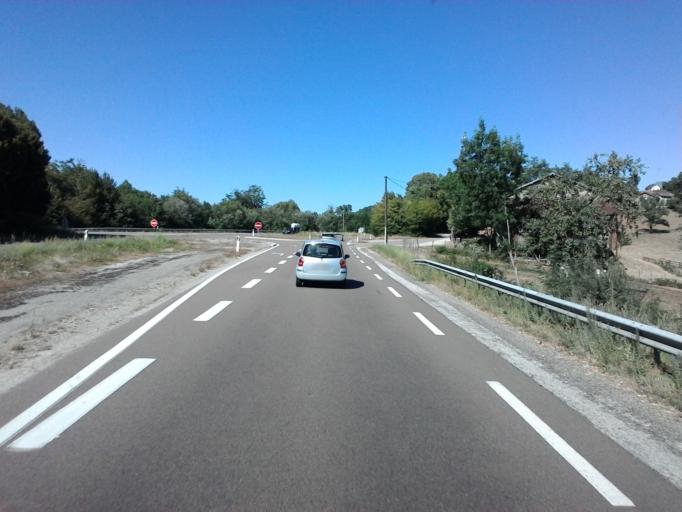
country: FR
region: Franche-Comte
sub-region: Departement du Doubs
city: Avanne-Aveney
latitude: 47.1663
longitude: 5.9567
